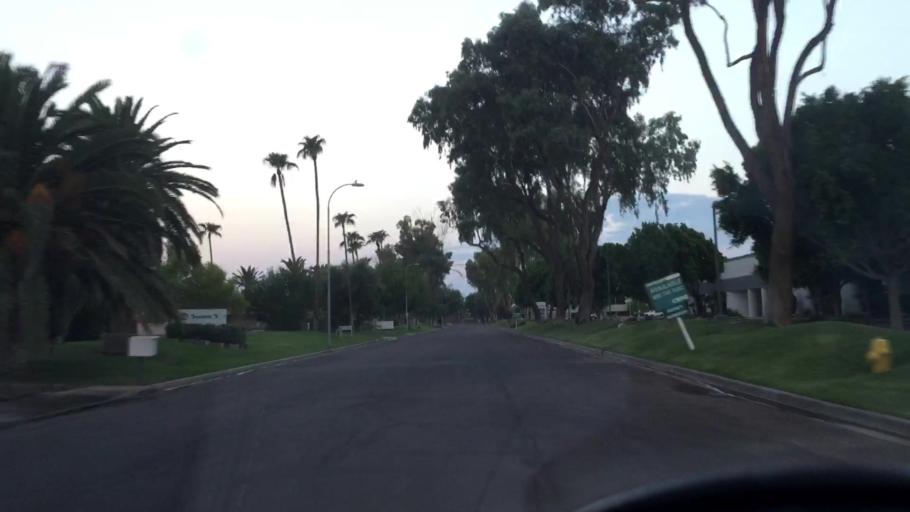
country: US
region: Arizona
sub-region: Maricopa County
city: Tempe Junction
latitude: 33.4098
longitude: -111.9637
